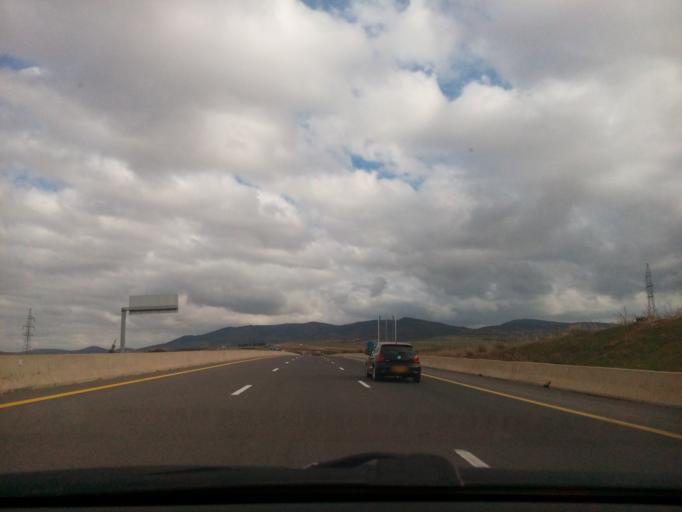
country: DZ
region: Tlemcen
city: Bensekrane
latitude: 34.9871
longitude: -1.2248
